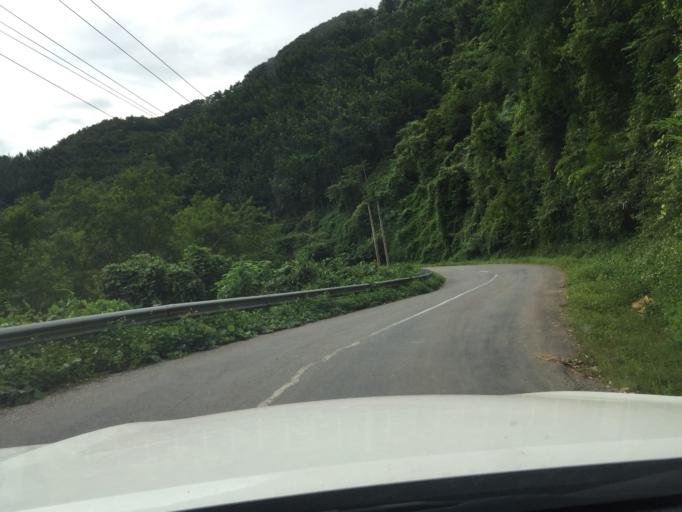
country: LA
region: Oudomxai
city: Muang La
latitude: 21.1048
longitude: 102.2276
